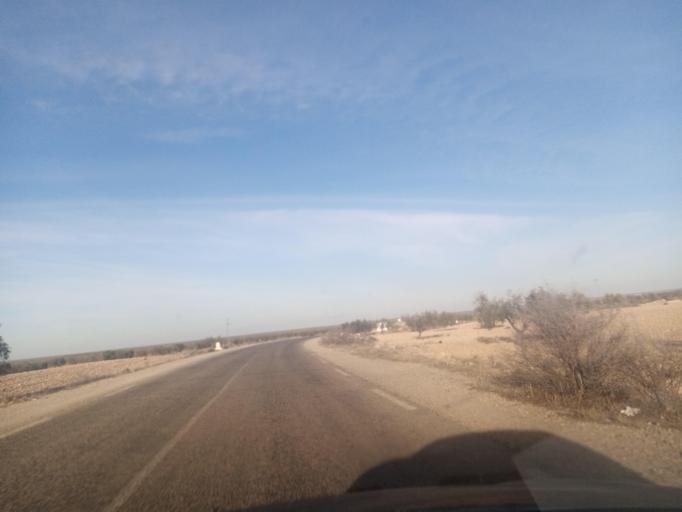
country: TN
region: Safaqis
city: Bi'r `Ali Bin Khalifah
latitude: 34.9287
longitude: 10.3231
